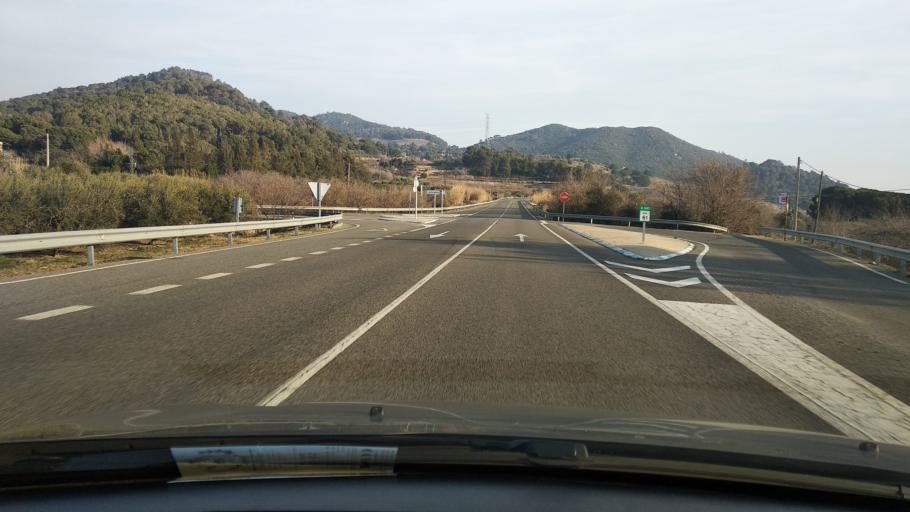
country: ES
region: Catalonia
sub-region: Provincia de Tarragona
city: Alforja
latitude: 41.2049
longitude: 0.9922
